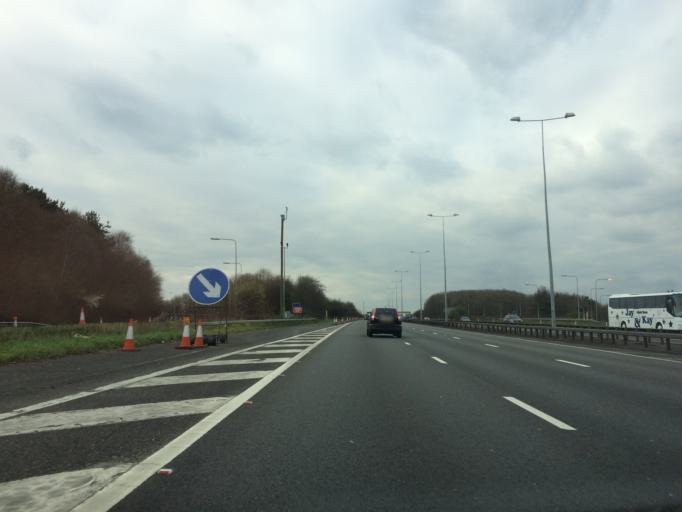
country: GB
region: England
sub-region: Surrey
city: Chertsey
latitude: 51.3967
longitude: -0.5354
